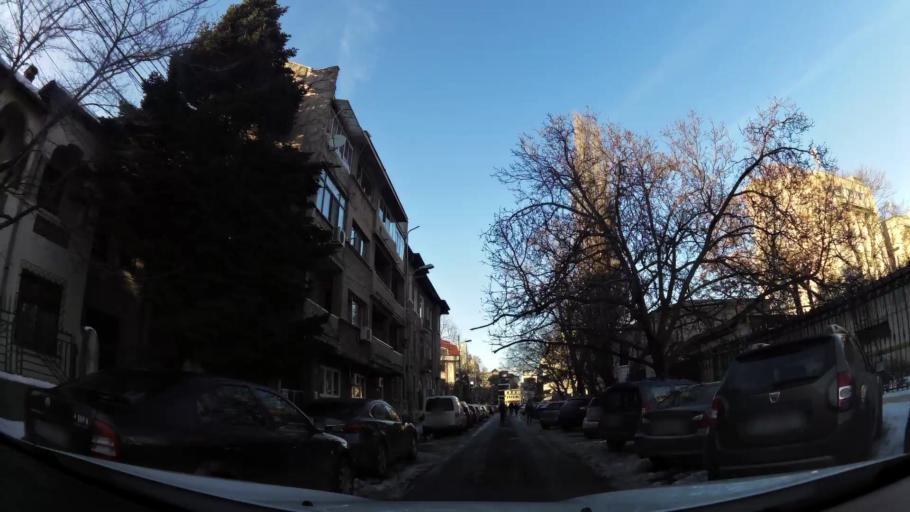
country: RO
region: Bucuresti
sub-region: Municipiul Bucuresti
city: Bucuresti
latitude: 44.4356
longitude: 26.0686
